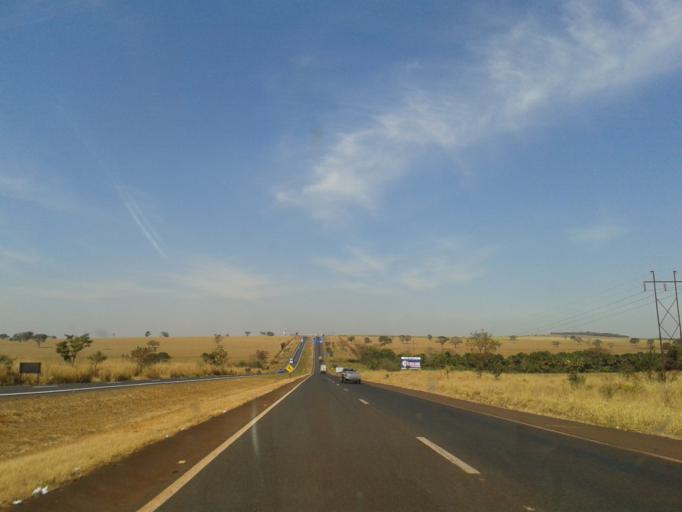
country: BR
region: Goias
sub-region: Itumbiara
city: Itumbiara
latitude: -18.2547
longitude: -49.2506
